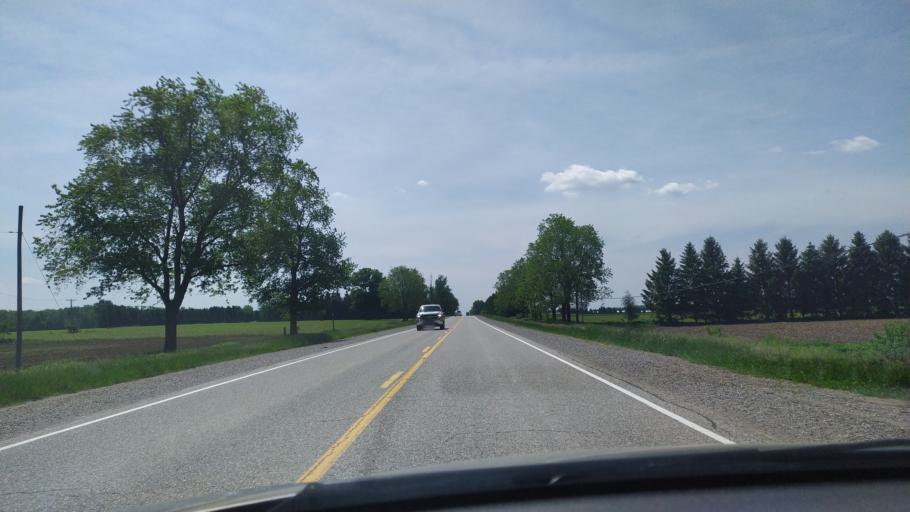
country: CA
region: Ontario
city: Dorchester
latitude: 43.1242
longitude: -81.0226
